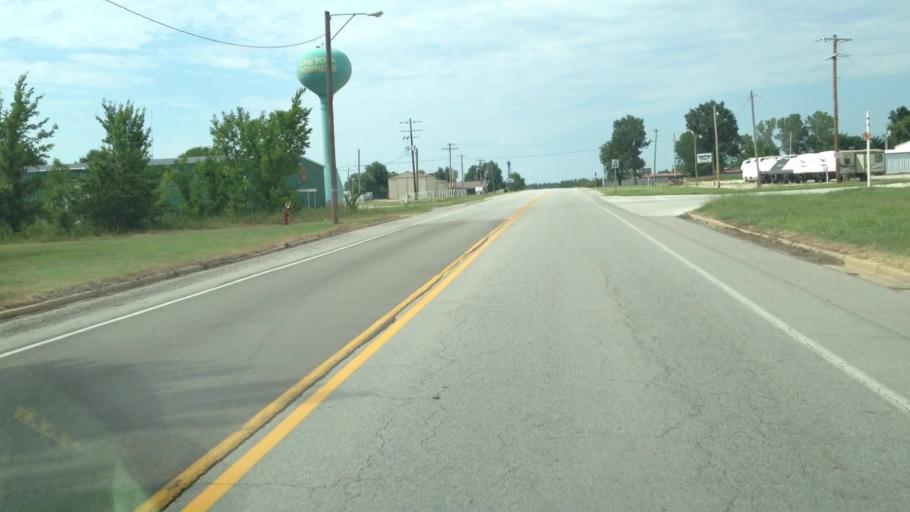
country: US
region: Kansas
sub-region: Labette County
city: Chetopa
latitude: 37.0402
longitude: -95.1002
